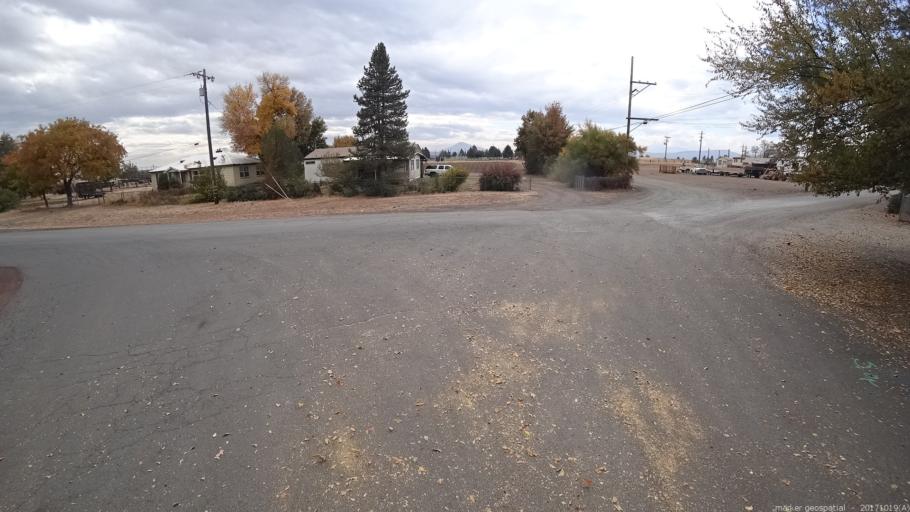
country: US
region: California
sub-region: Shasta County
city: Burney
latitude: 41.0464
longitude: -121.4029
